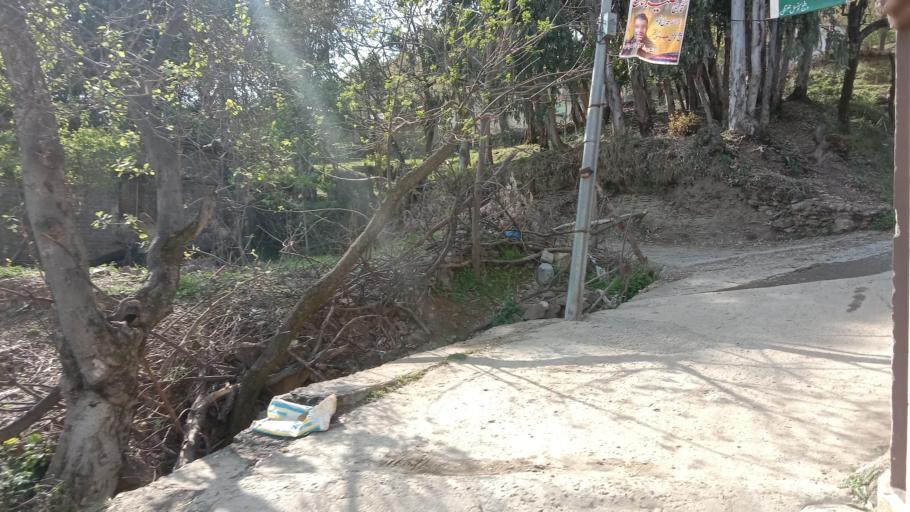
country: PK
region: Khyber Pakhtunkhwa
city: Abbottabad
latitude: 34.1772
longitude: 73.2093
